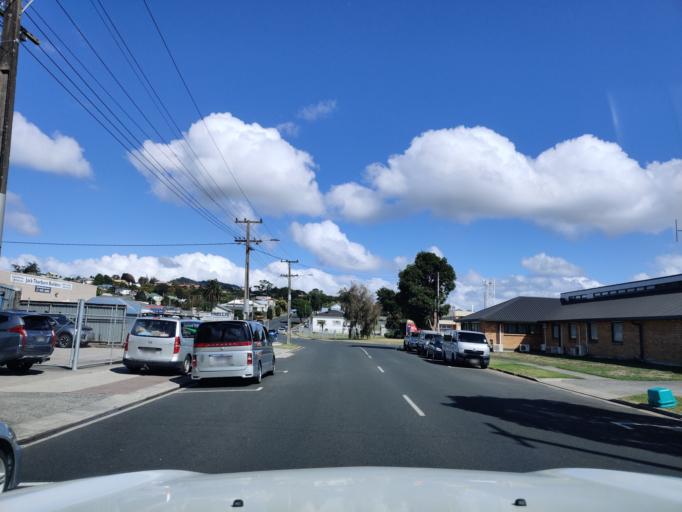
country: NZ
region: Waikato
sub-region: Waikato District
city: Ngaruawahia
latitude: -37.5590
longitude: 175.1612
